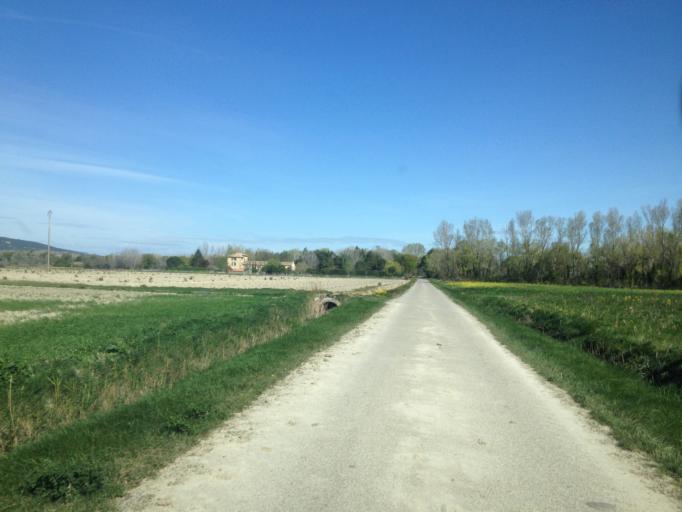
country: FR
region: Provence-Alpes-Cote d'Azur
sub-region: Departement du Vaucluse
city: Caderousse
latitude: 44.1301
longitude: 4.7540
